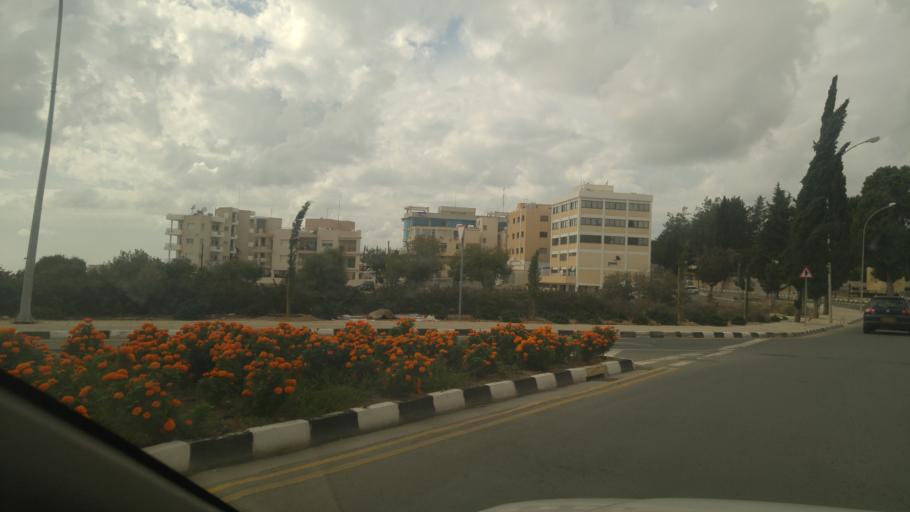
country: CY
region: Pafos
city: Paphos
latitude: 34.7707
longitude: 32.4329
